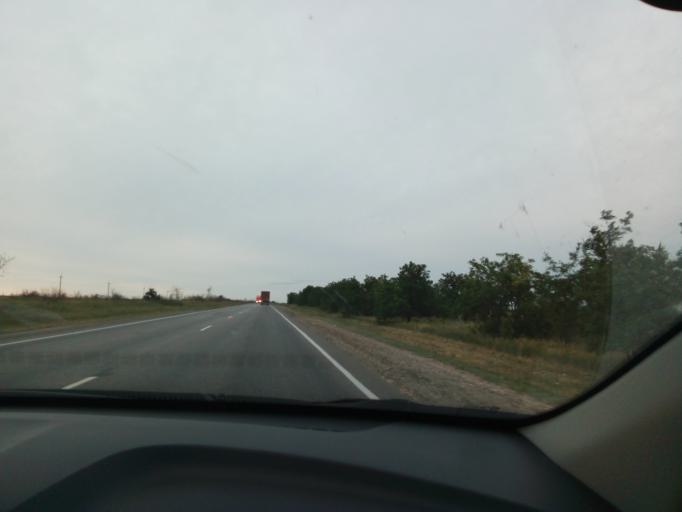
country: RU
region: Volgograd
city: Dubovka
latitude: 49.1427
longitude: 44.8288
